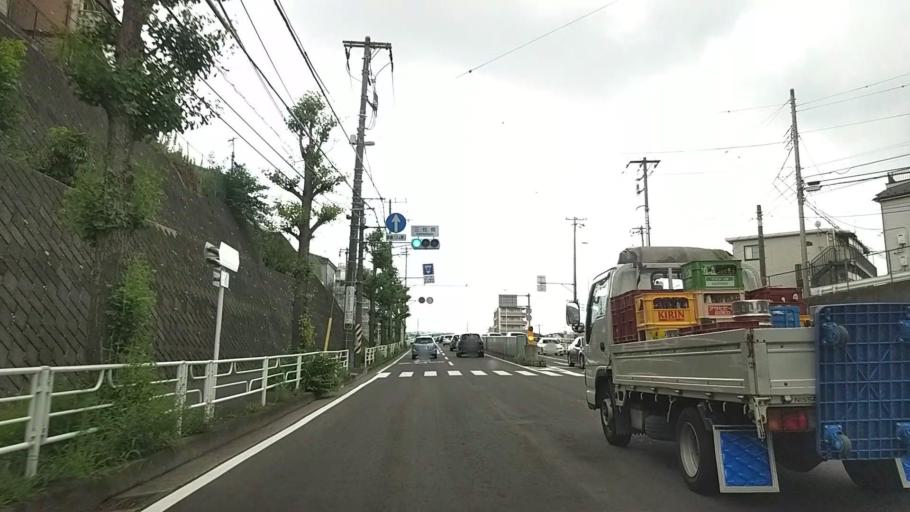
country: JP
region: Kanagawa
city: Yokohama
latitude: 35.4952
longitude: 139.6075
